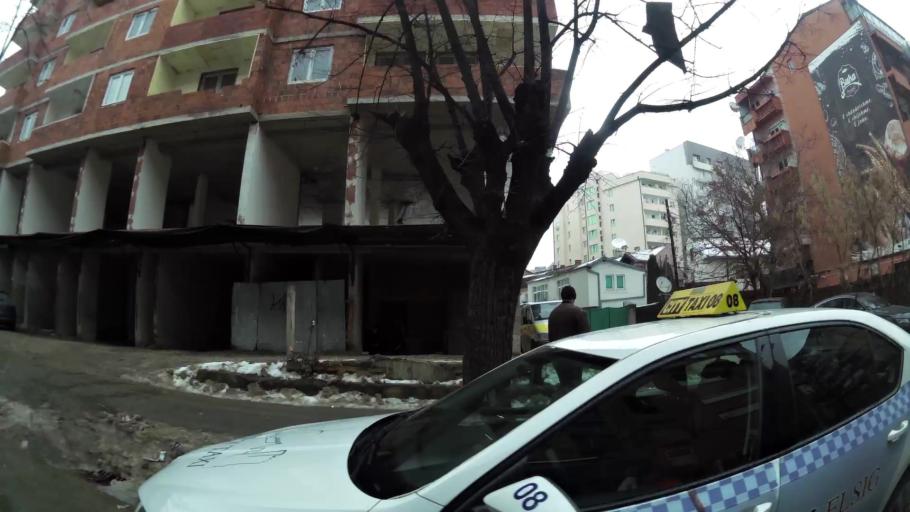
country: XK
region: Pristina
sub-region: Komuna e Prishtines
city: Pristina
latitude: 42.6654
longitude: 21.1580
